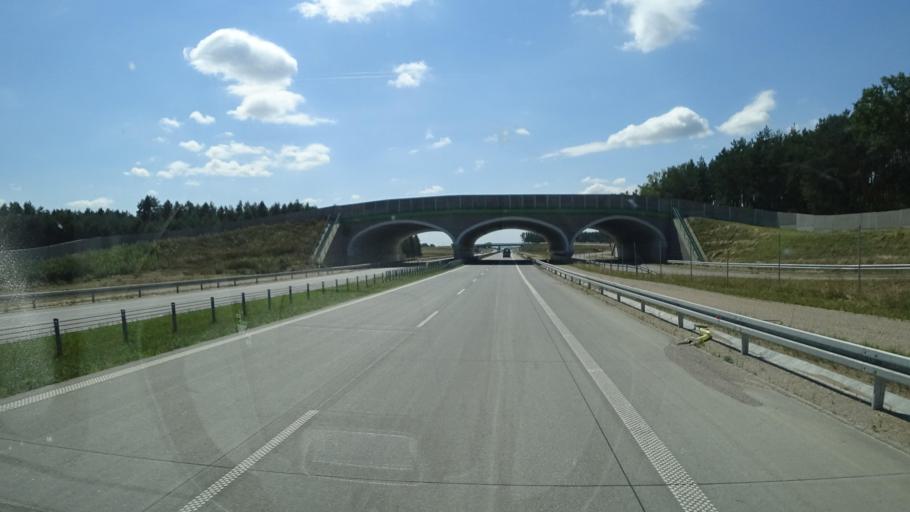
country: PL
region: Podlasie
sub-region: Powiat kolnenski
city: Stawiski
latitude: 53.2872
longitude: 22.1428
